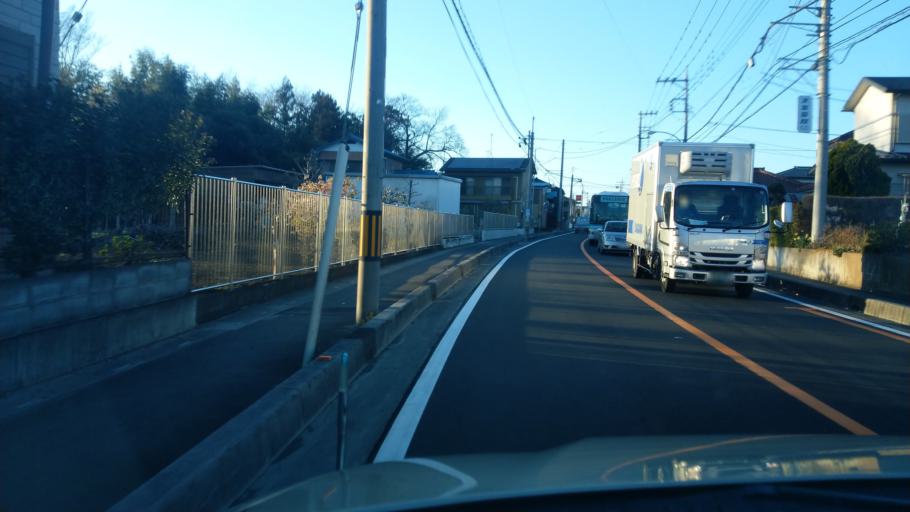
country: JP
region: Saitama
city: Ageoshimo
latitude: 35.9283
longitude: 139.5583
